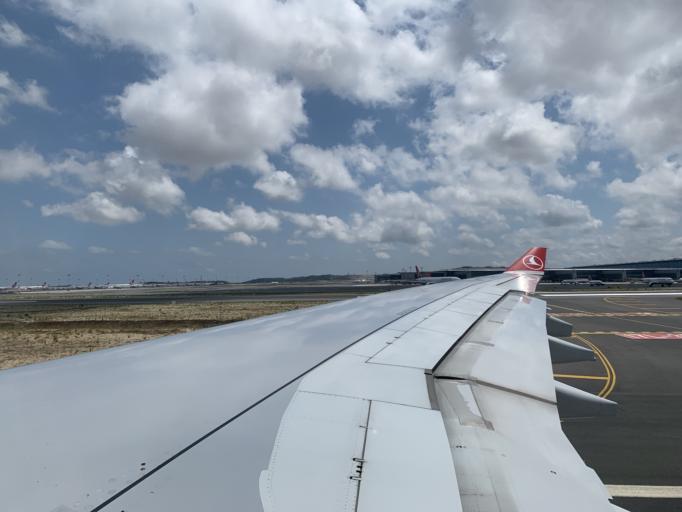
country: TR
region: Istanbul
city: Durusu
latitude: 41.2674
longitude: 28.7253
